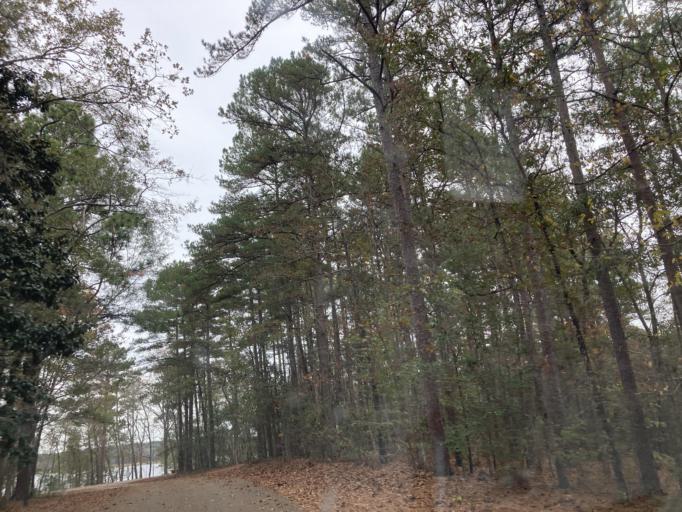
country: US
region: Mississippi
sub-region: Lamar County
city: Lumberton
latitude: 31.0828
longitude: -89.4942
